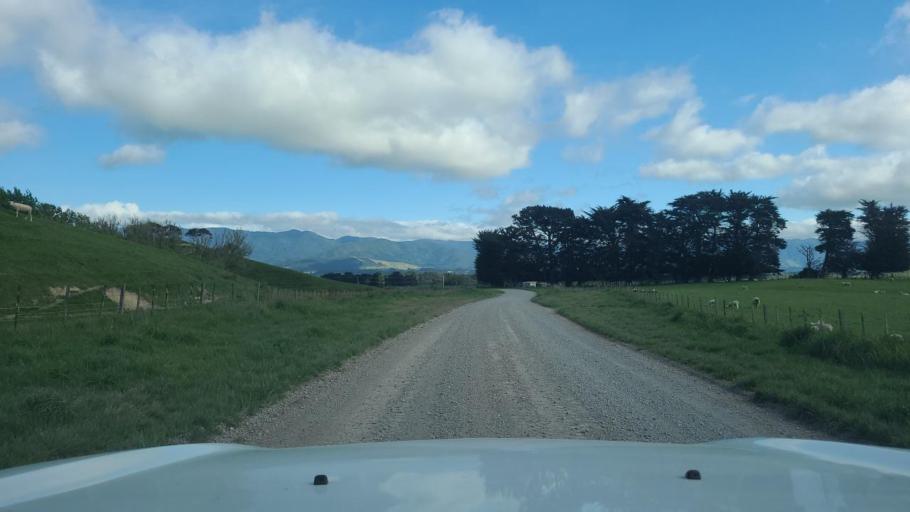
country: NZ
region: Wellington
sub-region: Upper Hutt City
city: Upper Hutt
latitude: -41.3395
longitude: 175.2018
